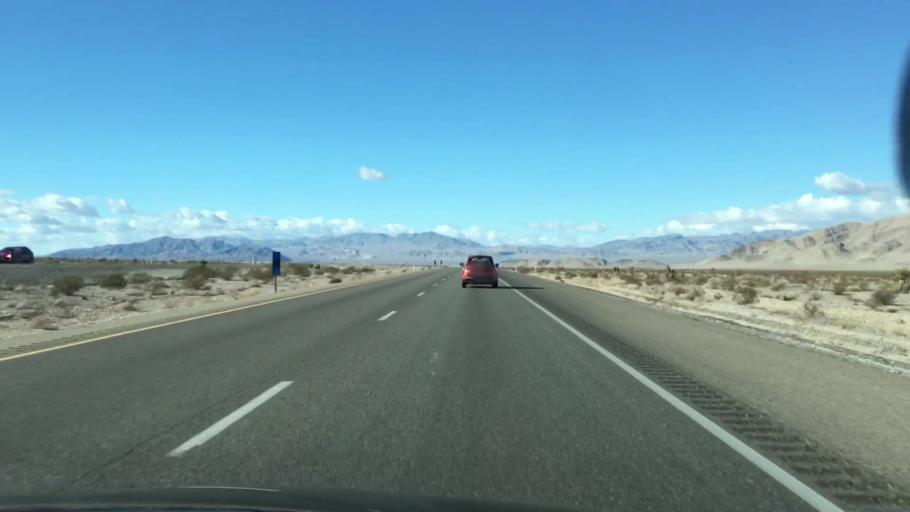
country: US
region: Nevada
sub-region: Nye County
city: Pahrump
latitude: 36.5589
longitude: -115.6085
